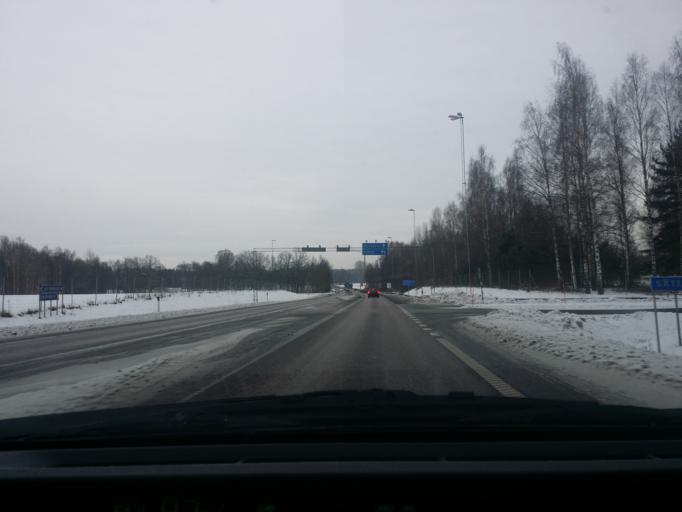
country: SE
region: Vaestra Goetaland
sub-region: Skovde Kommun
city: Stopen
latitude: 58.4523
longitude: 13.8490
